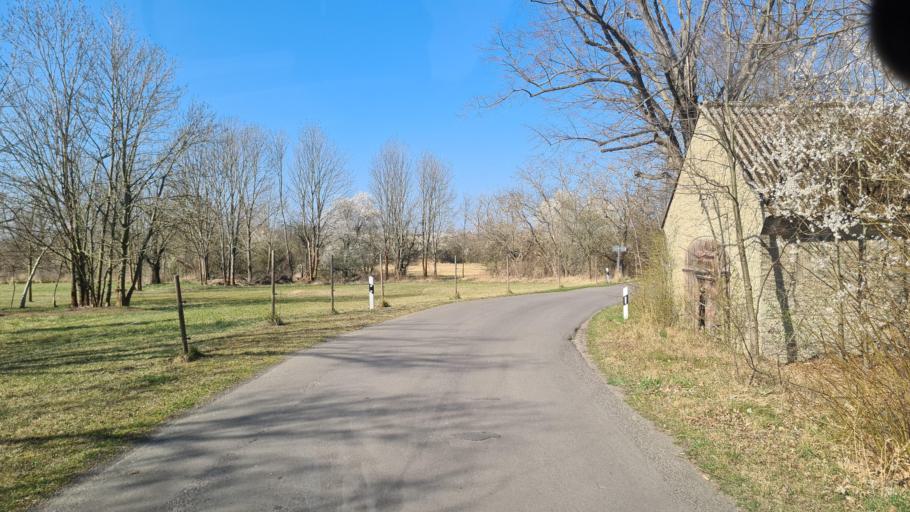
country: DE
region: Brandenburg
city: Calau
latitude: 51.7885
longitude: 14.0061
